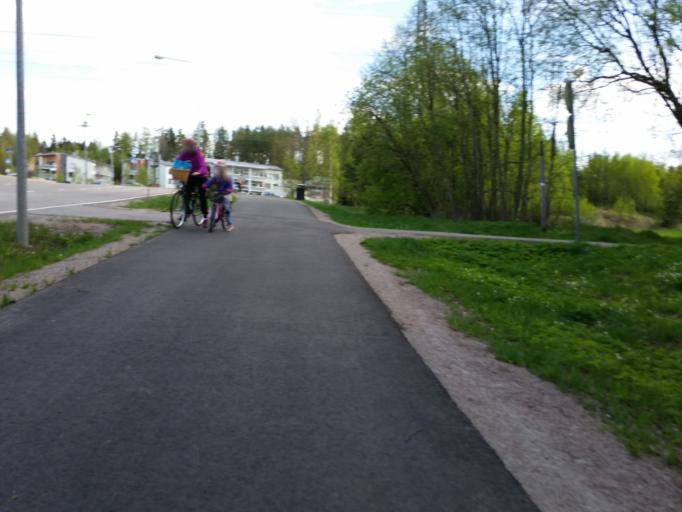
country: FI
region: Uusimaa
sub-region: Helsinki
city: Espoo
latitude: 60.2163
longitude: 24.6247
